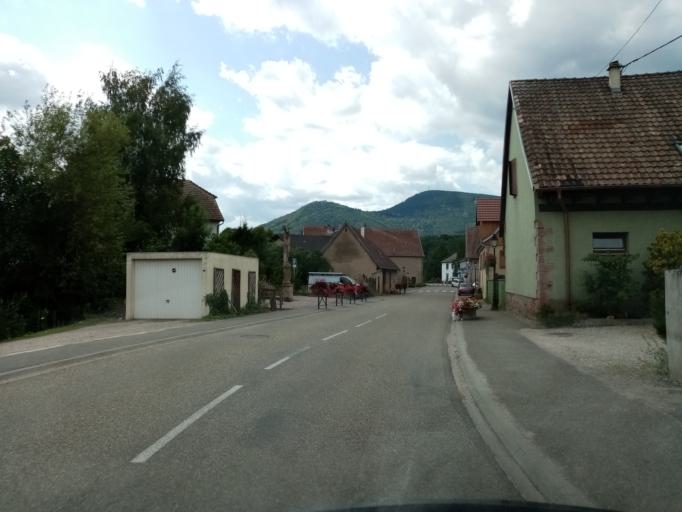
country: FR
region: Alsace
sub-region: Departement du Bas-Rhin
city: Ville
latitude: 48.3211
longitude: 7.3506
